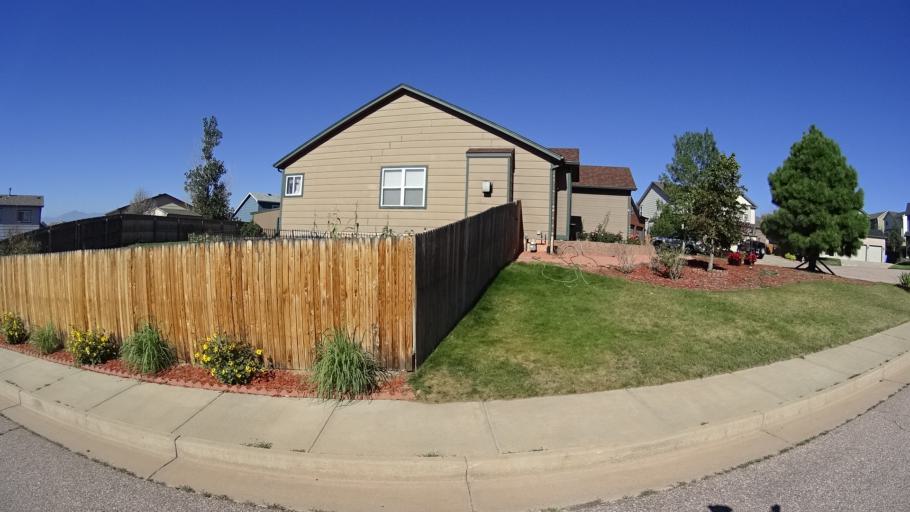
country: US
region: Colorado
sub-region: El Paso County
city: Black Forest
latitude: 38.9450
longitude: -104.7349
